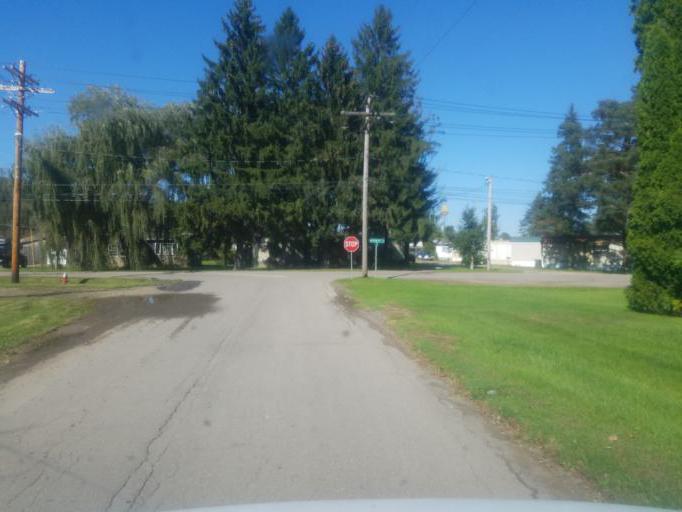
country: US
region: New York
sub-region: Allegany County
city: Cuba
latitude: 42.2201
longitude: -78.2801
